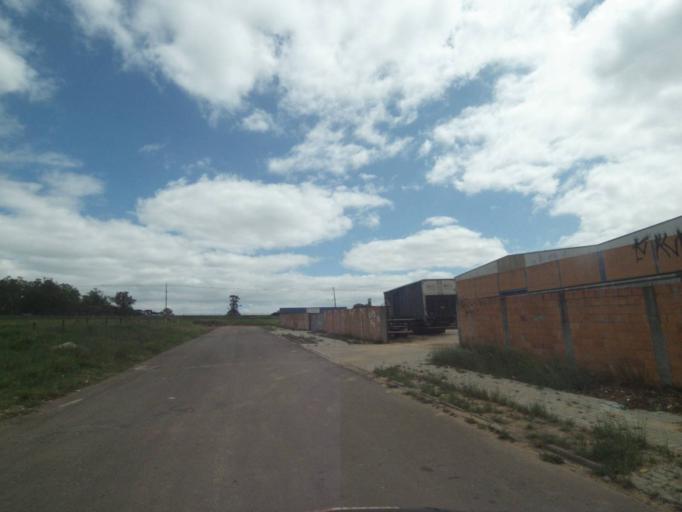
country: BR
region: Parana
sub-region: Sao Jose Dos Pinhais
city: Sao Jose dos Pinhais
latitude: -25.5577
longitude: -49.2665
